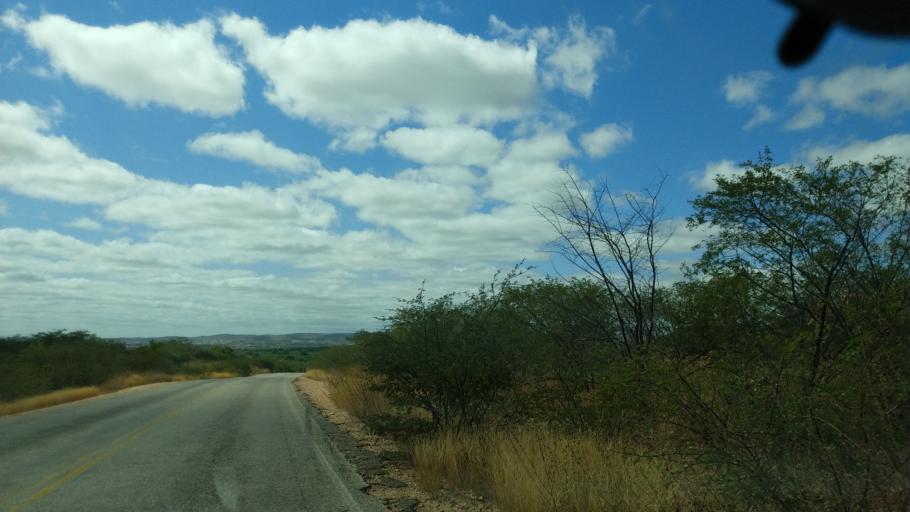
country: BR
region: Rio Grande do Norte
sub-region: Currais Novos
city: Currais Novos
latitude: -6.2609
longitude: -36.5739
